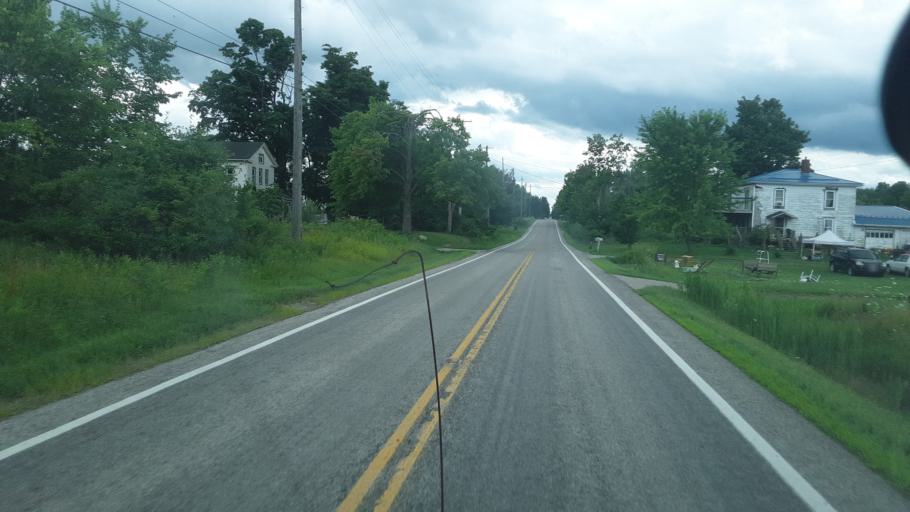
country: US
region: Ohio
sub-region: Ashtabula County
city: Jefferson
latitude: 41.6904
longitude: -80.7812
